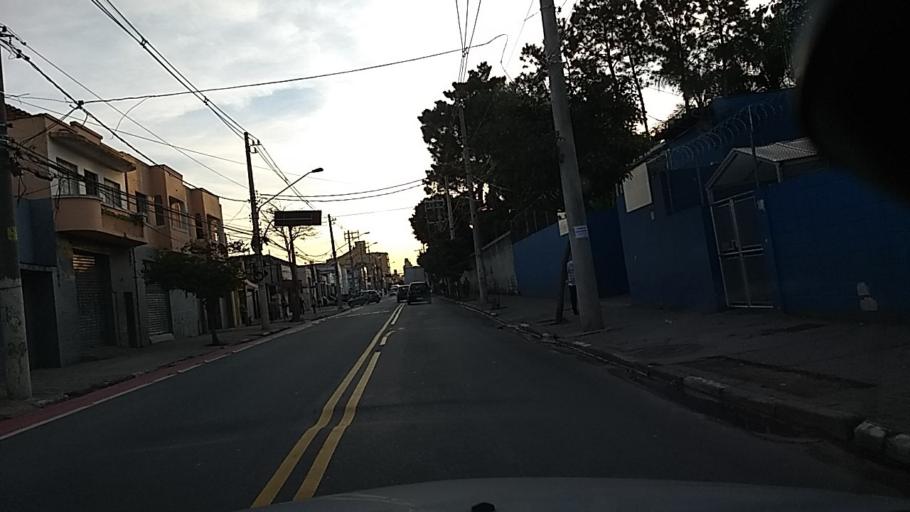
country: BR
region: Sao Paulo
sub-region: Sao Paulo
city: Sao Paulo
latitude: -23.5255
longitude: -46.6234
